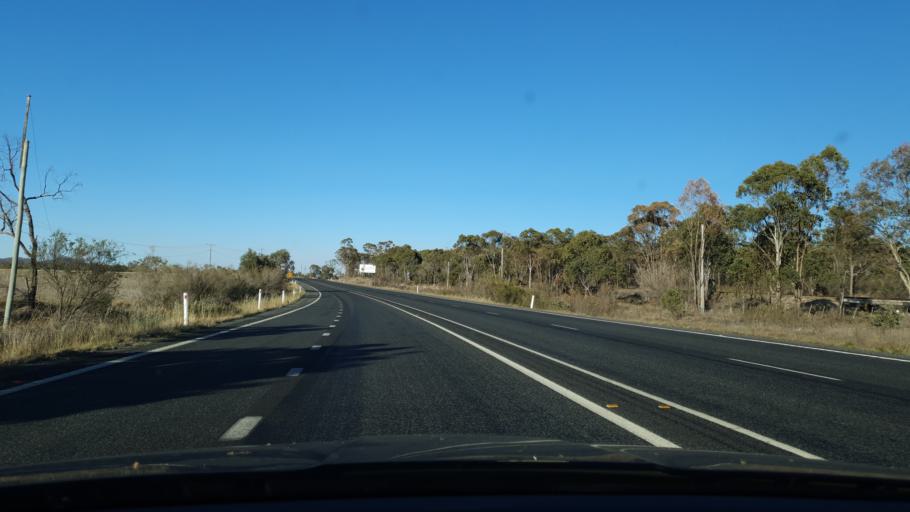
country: AU
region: Queensland
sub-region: Southern Downs
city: Stanthorpe
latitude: -28.6887
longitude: 151.9108
